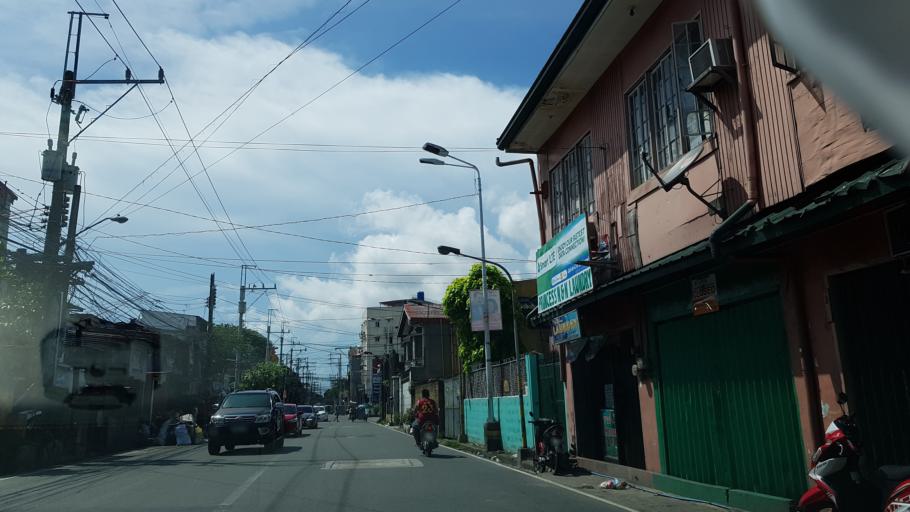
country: PH
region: Metro Manila
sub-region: Mandaluyong
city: Mandaluyong City
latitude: 14.5778
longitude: 121.0103
